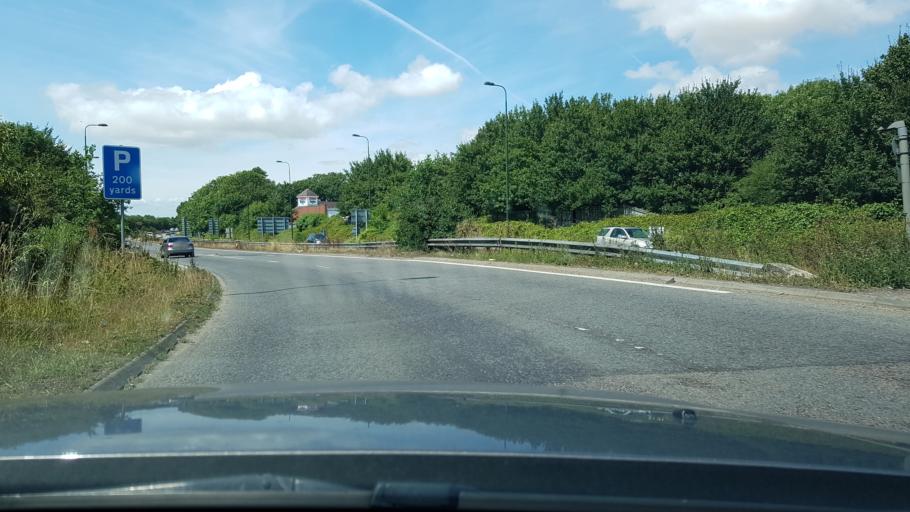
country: GB
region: England
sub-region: West Sussex
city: Chichester
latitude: 50.8330
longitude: -0.7996
